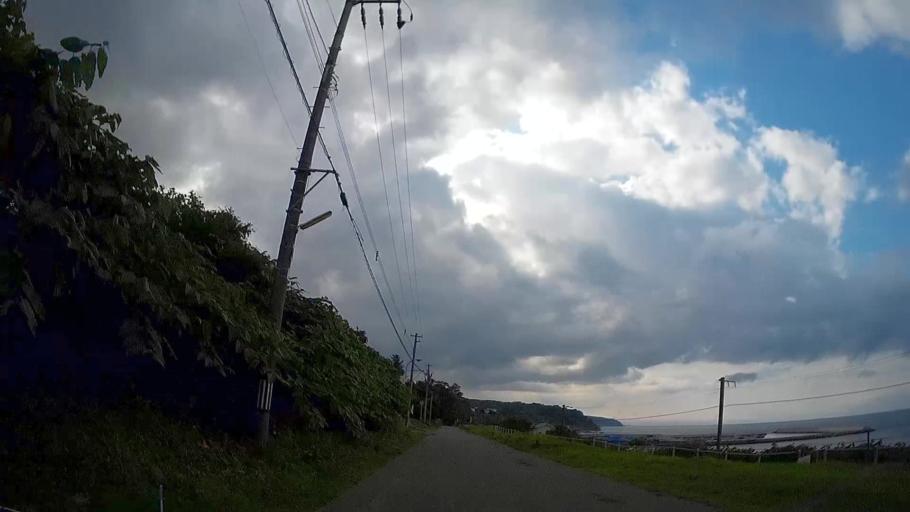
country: JP
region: Hokkaido
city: Nanae
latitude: 42.1127
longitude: 140.5494
